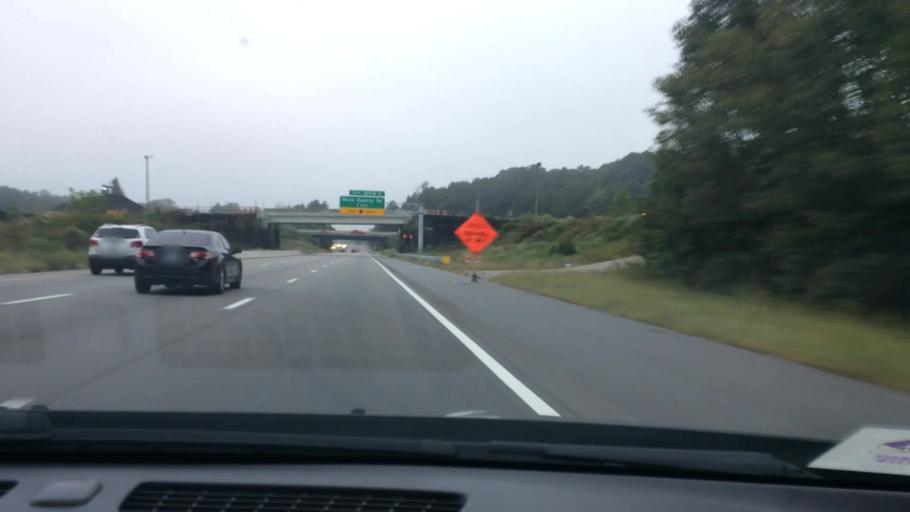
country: US
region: North Carolina
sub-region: Wake County
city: Garner
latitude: 35.7538
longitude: -78.5907
